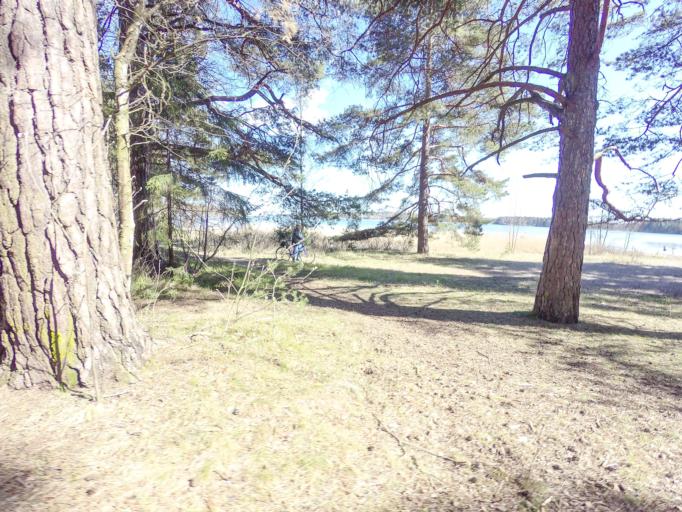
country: FI
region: Uusimaa
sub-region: Helsinki
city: Vantaa
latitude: 60.1787
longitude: 25.0659
